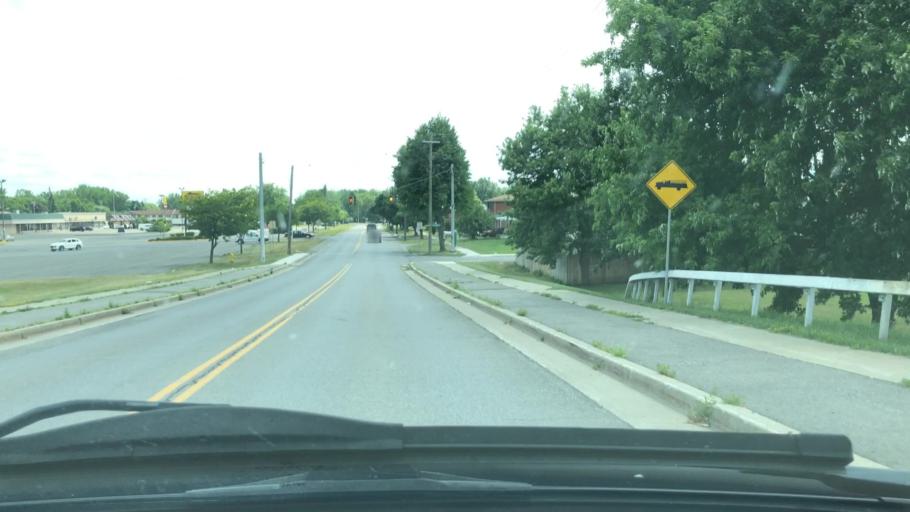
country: US
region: New York
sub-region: Erie County
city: Sloan
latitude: 42.8752
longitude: -78.7949
